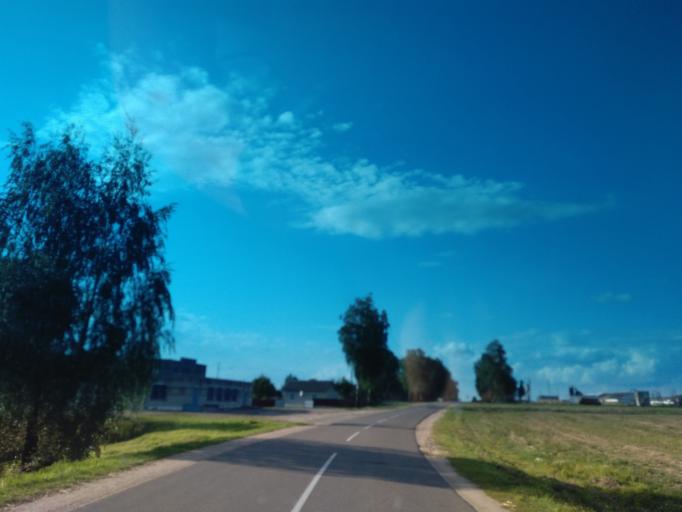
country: BY
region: Minsk
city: Kapyl'
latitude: 53.2598
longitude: 26.9578
